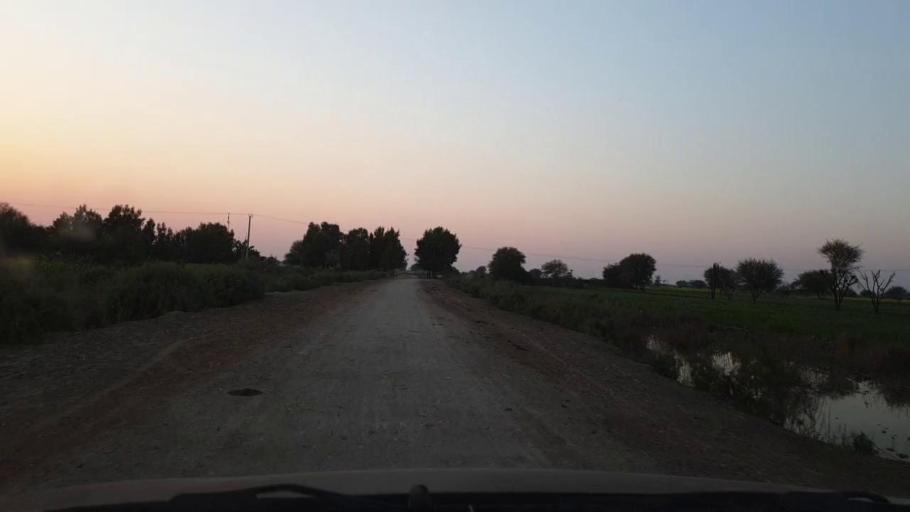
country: PK
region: Sindh
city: Jhol
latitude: 25.9375
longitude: 68.9590
